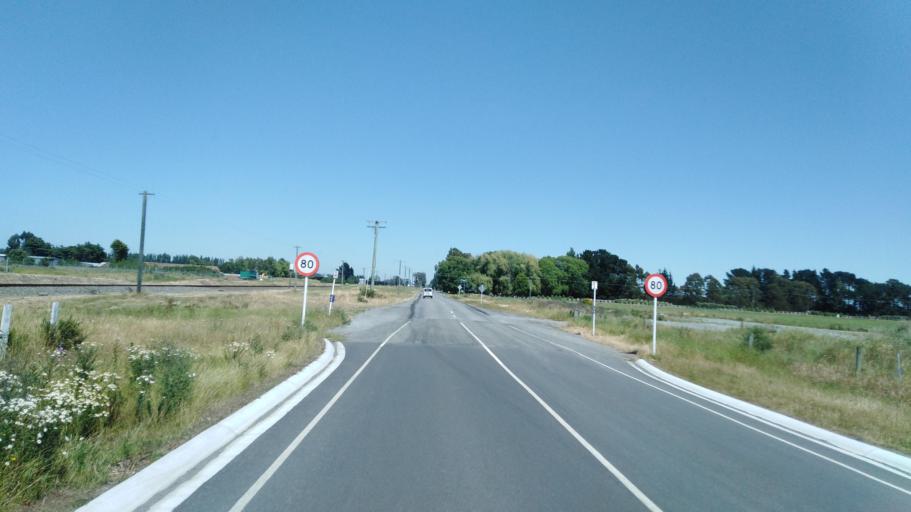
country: NZ
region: Canterbury
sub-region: Selwyn District
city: Rolleston
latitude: -43.5659
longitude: 172.4430
